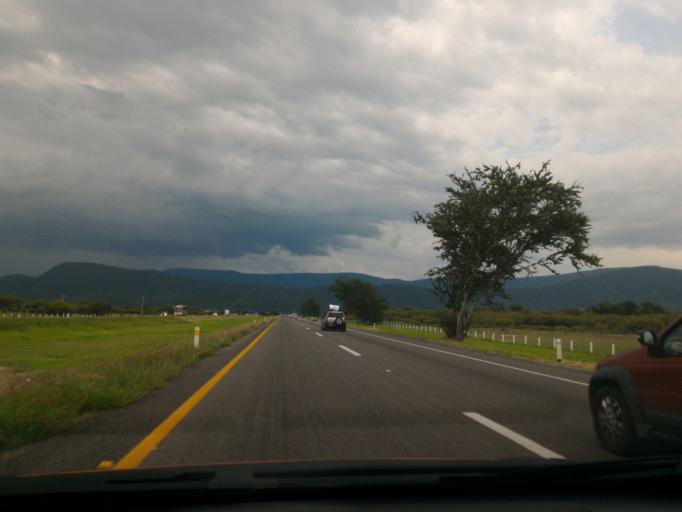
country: MX
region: Jalisco
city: Zacoalco de Torres
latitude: 20.1500
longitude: -103.5030
